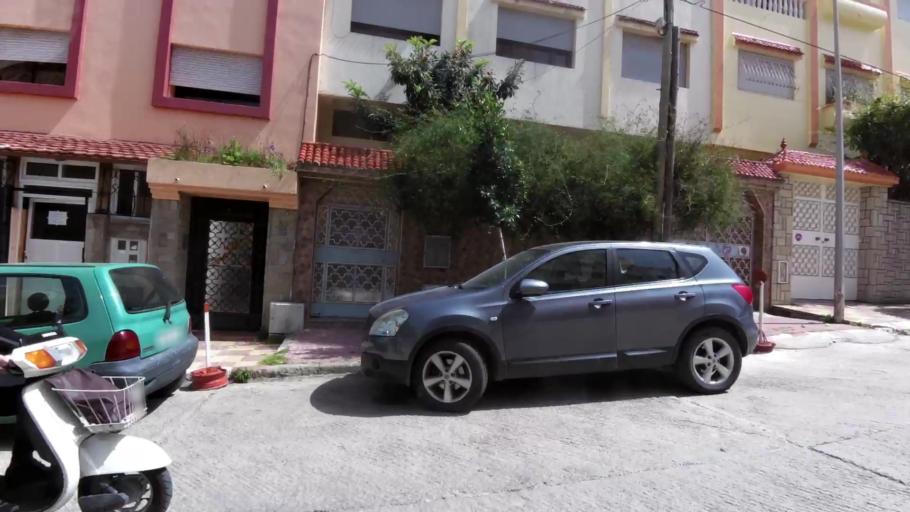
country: MA
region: Tanger-Tetouan
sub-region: Tanger-Assilah
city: Tangier
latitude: 35.7594
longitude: -5.8333
